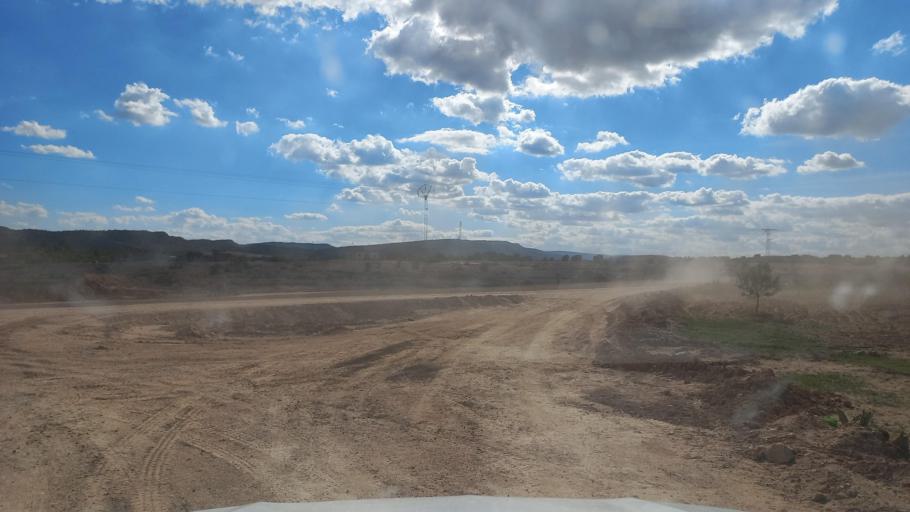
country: TN
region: Al Qasrayn
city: Sbiba
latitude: 35.4028
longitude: 8.9994
